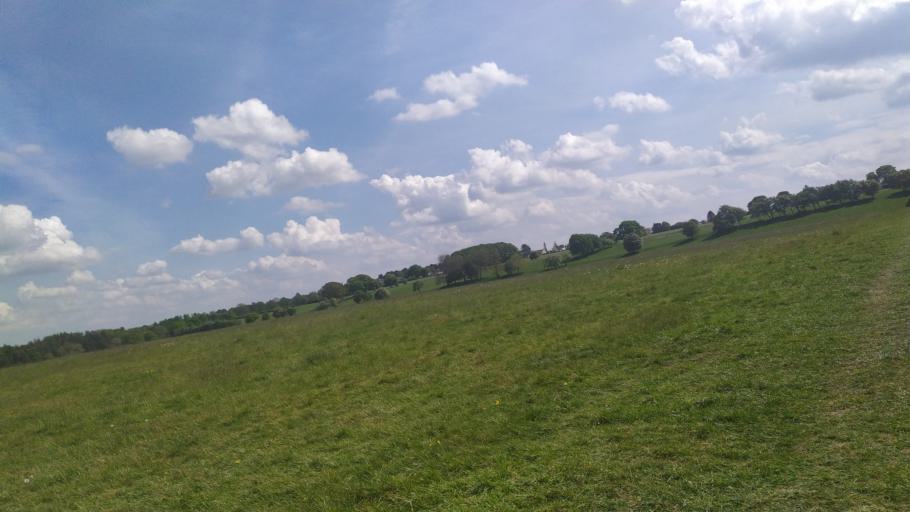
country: GB
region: England
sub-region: City and Borough of Leeds
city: Chapel Allerton
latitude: 53.8683
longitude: -1.5610
